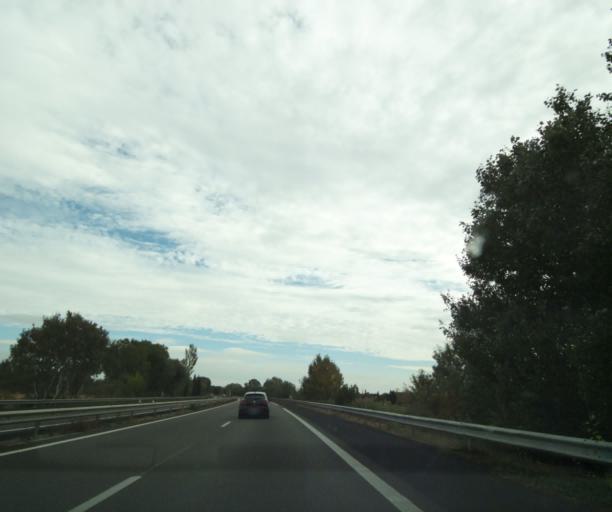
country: FR
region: Languedoc-Roussillon
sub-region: Departement du Gard
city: Bellegarde
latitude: 43.7129
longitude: 4.5143
